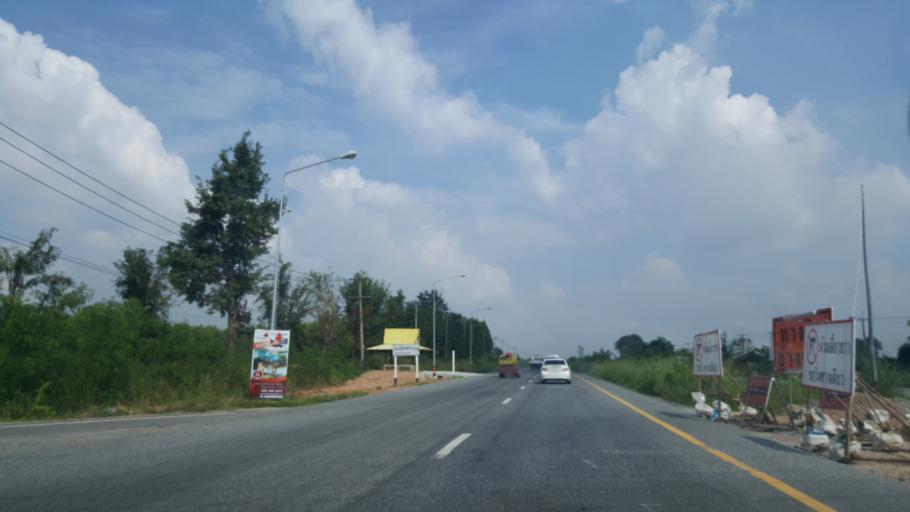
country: TH
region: Chon Buri
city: Phatthaya
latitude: 12.8773
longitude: 101.0233
